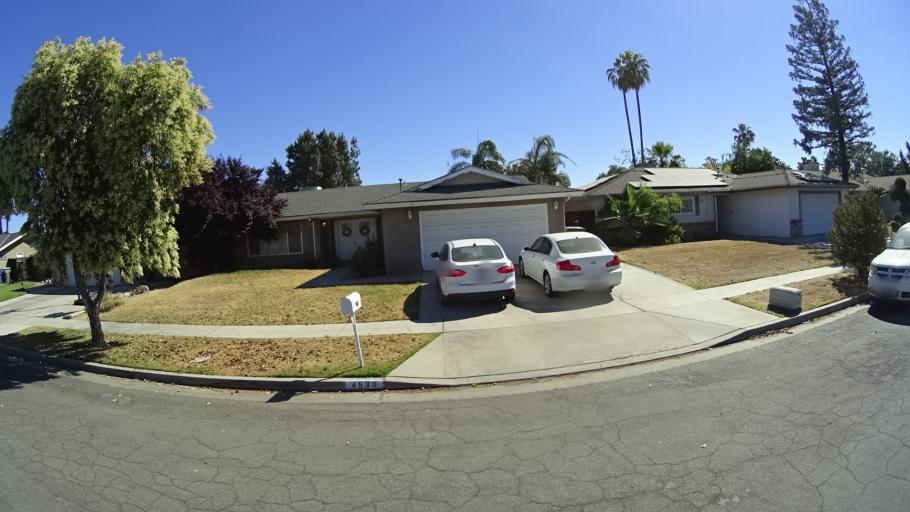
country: US
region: California
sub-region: Fresno County
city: Fresno
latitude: 36.7993
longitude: -119.8301
